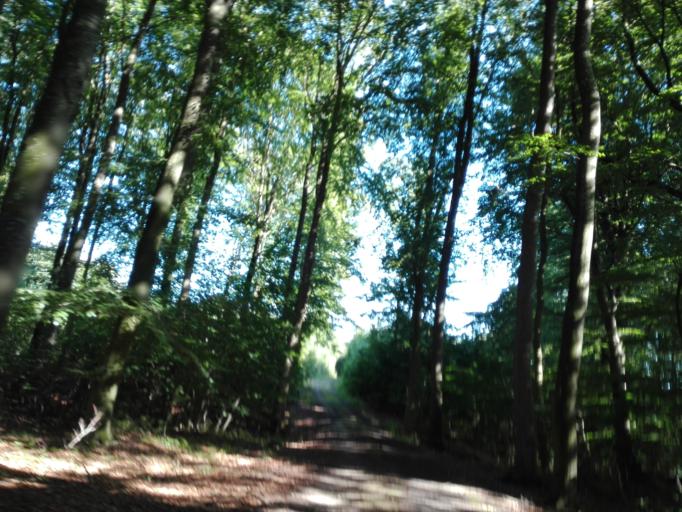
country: DK
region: Central Jutland
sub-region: Odder Kommune
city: Odder
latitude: 55.9536
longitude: 10.0787
